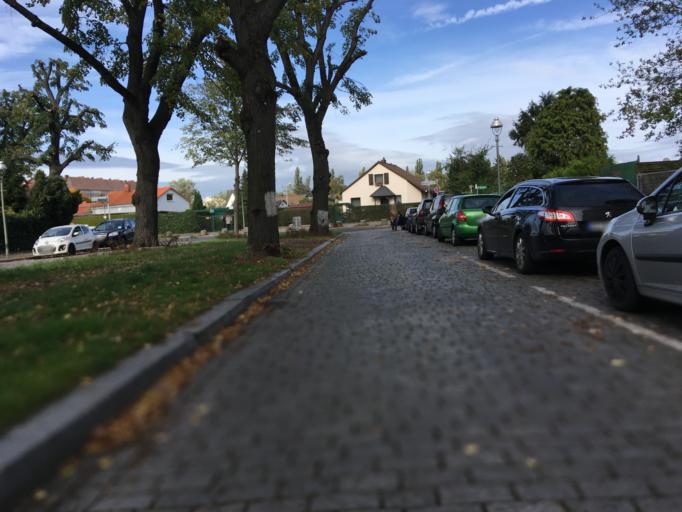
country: DE
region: Berlin
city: Gesundbrunnen
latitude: 52.5519
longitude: 13.3955
